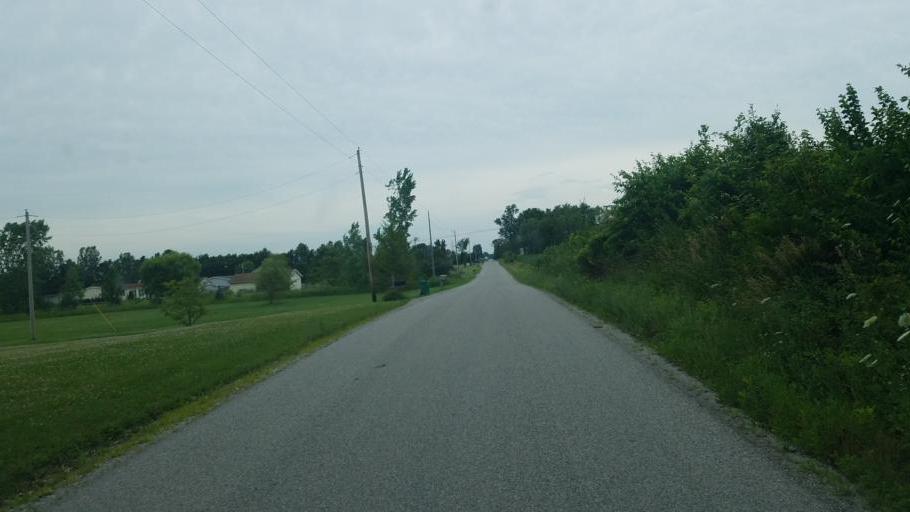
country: US
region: Ohio
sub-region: Knox County
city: Centerburg
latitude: 40.2497
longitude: -82.6054
